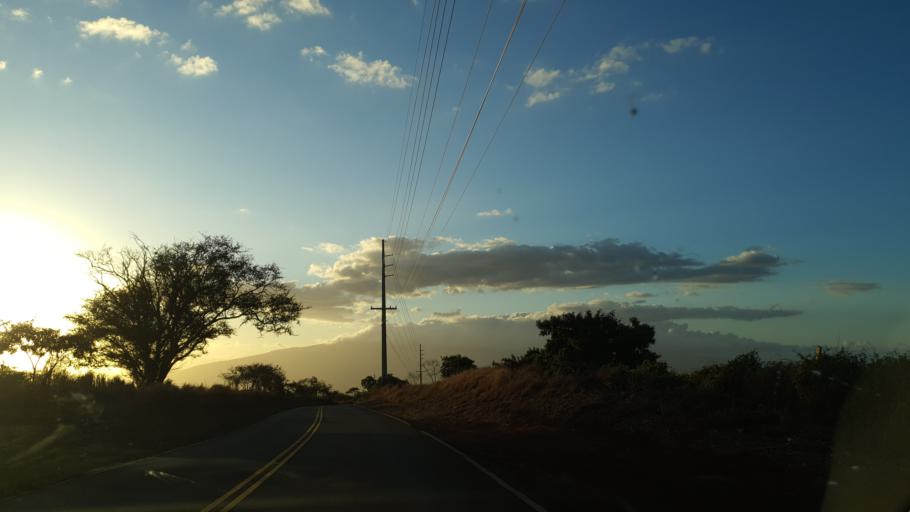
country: US
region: Hawaii
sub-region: Maui County
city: Pukalani
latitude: 20.7903
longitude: -156.3552
